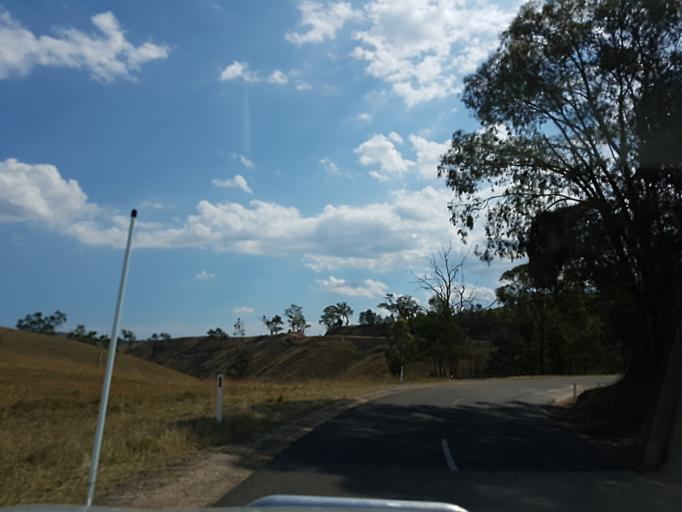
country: AU
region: Victoria
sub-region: East Gippsland
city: Lakes Entrance
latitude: -37.4987
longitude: 148.1938
